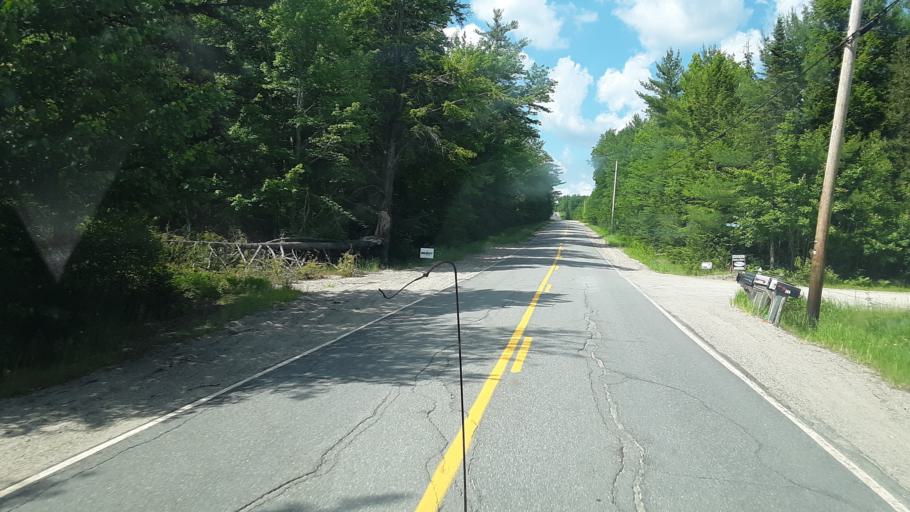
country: US
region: Maine
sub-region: Washington County
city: Machias
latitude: 44.9347
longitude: -67.6635
